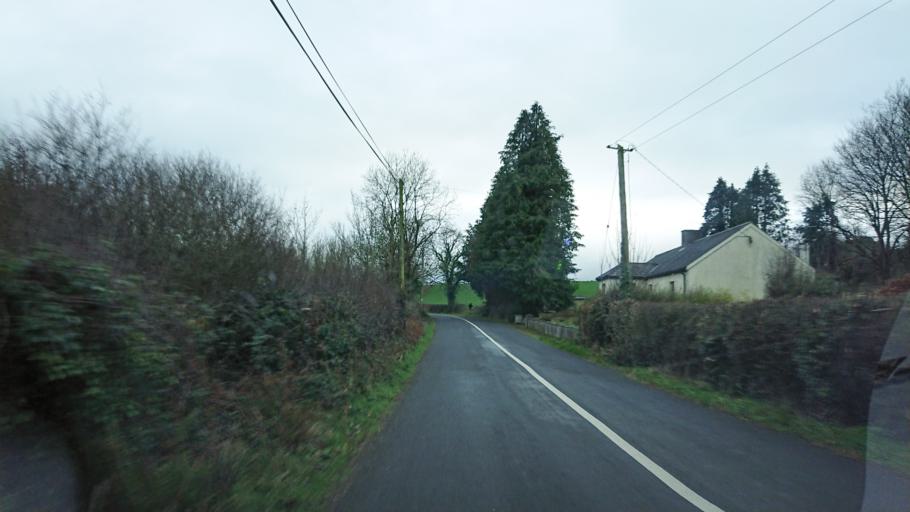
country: IE
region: Munster
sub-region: Waterford
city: Portlaw
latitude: 52.2735
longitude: -7.3905
